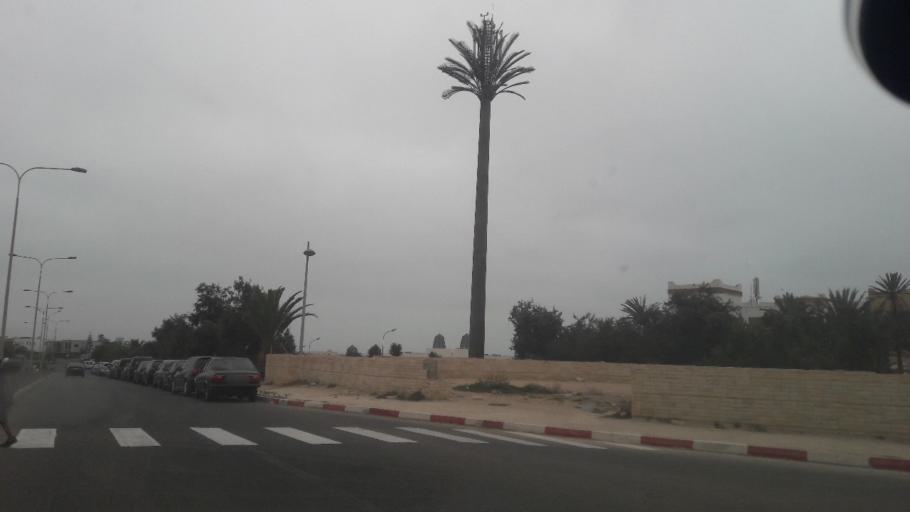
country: MA
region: Souss-Massa-Draa
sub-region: Agadir-Ida-ou-Tnan
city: Agadir
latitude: 30.3955
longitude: -9.5951
